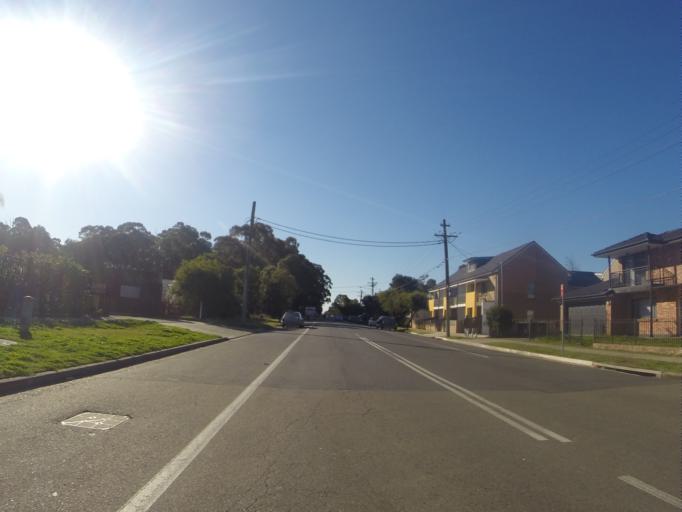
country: AU
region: New South Wales
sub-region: Bankstown
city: Regents Park
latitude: -33.8716
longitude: 151.0170
